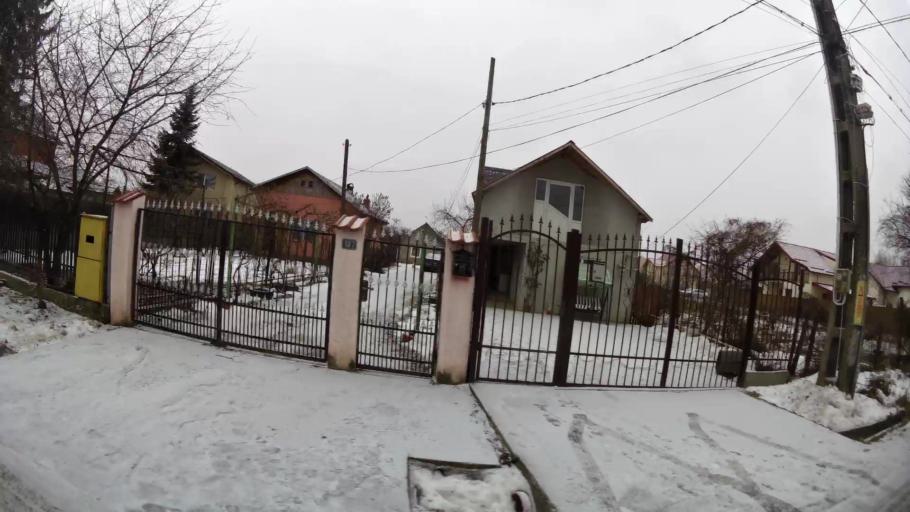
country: RO
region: Dambovita
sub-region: Comuna Aninoasa
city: Viforata
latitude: 44.9445
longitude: 25.4692
